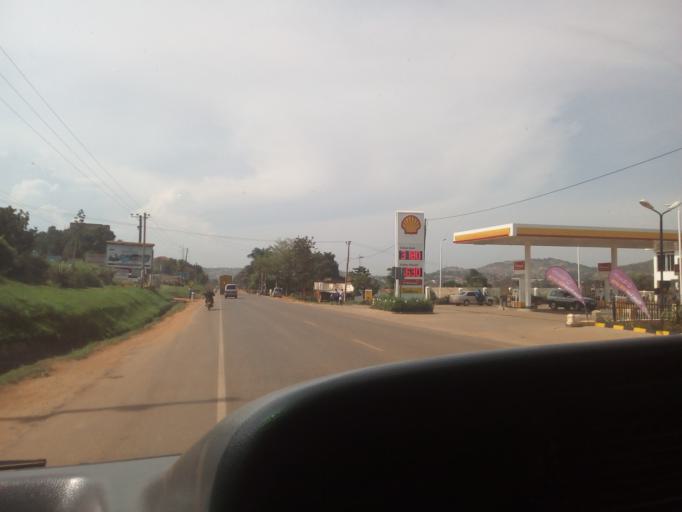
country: UG
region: Central Region
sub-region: Wakiso District
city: Kajansi
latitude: 0.1998
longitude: 32.5399
